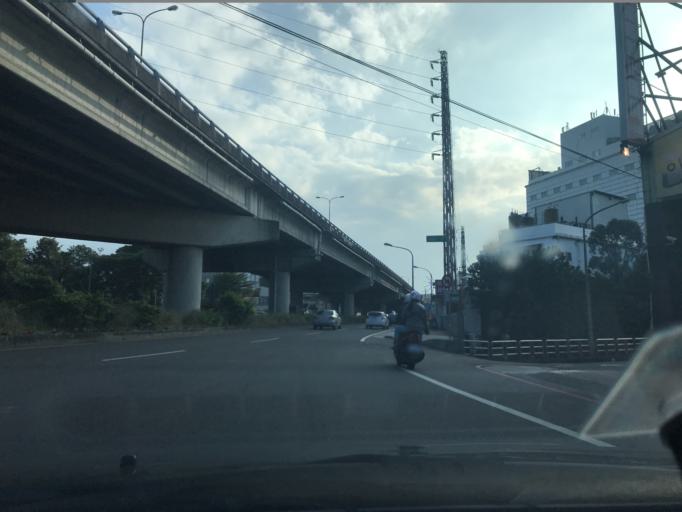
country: TW
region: Taiwan
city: Taoyuan City
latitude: 24.9865
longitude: 121.2385
